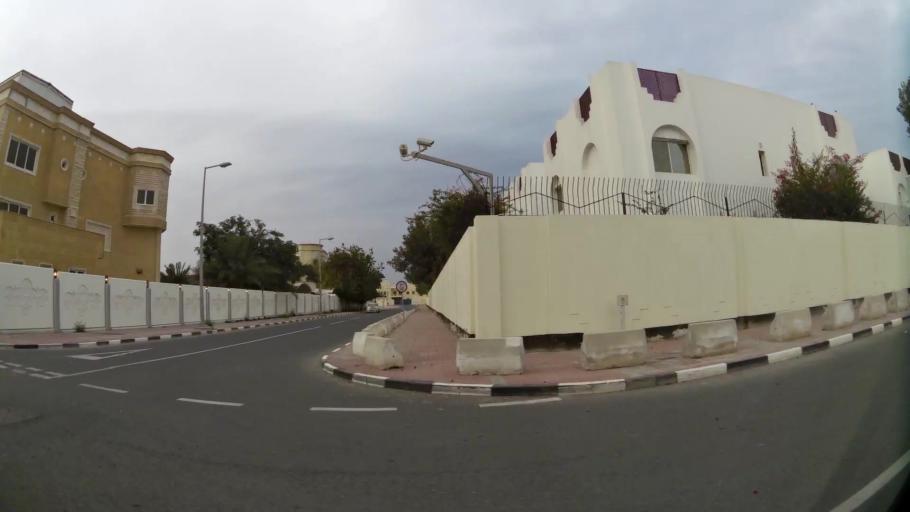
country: QA
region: Baladiyat ad Dawhah
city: Doha
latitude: 25.3263
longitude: 51.5115
